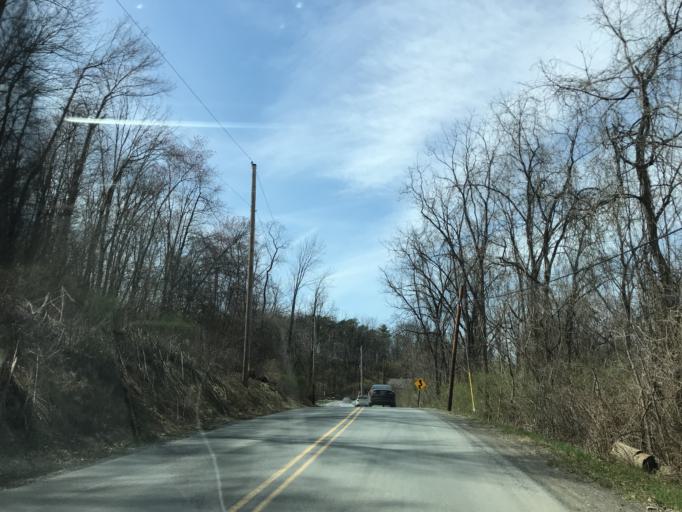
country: US
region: Pennsylvania
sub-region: Northumberland County
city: Northumberland
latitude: 40.9006
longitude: -76.8421
